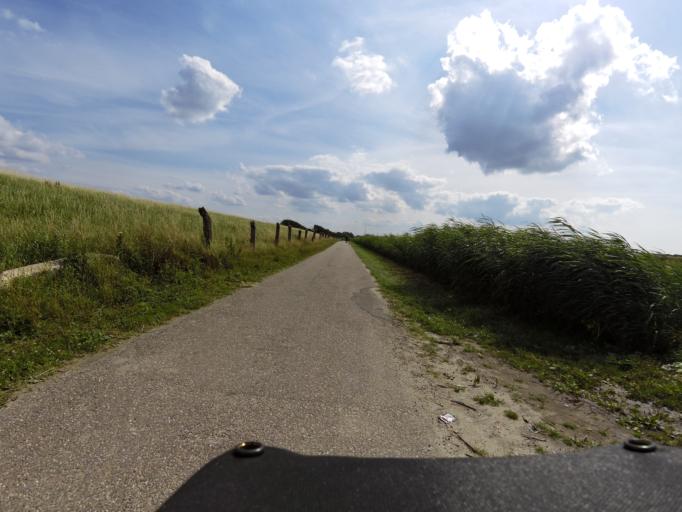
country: NL
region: South Holland
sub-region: Gemeente Goeree-Overflakkee
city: Ouddorp
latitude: 51.8222
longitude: 3.8970
